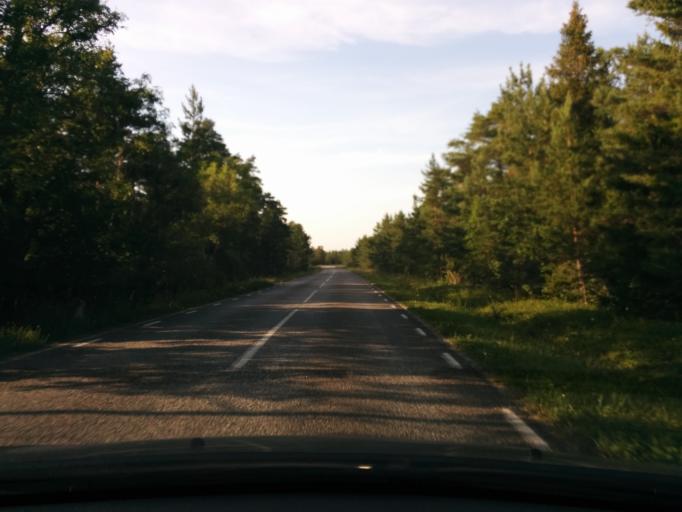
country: SE
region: Gotland
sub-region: Gotland
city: Slite
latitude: 57.5292
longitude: 18.6970
